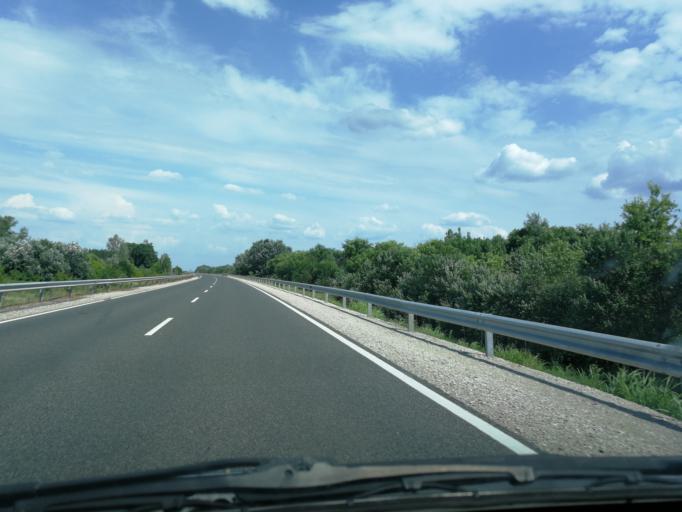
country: HU
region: Tolna
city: Tolna
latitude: 46.3761
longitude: 18.7790
